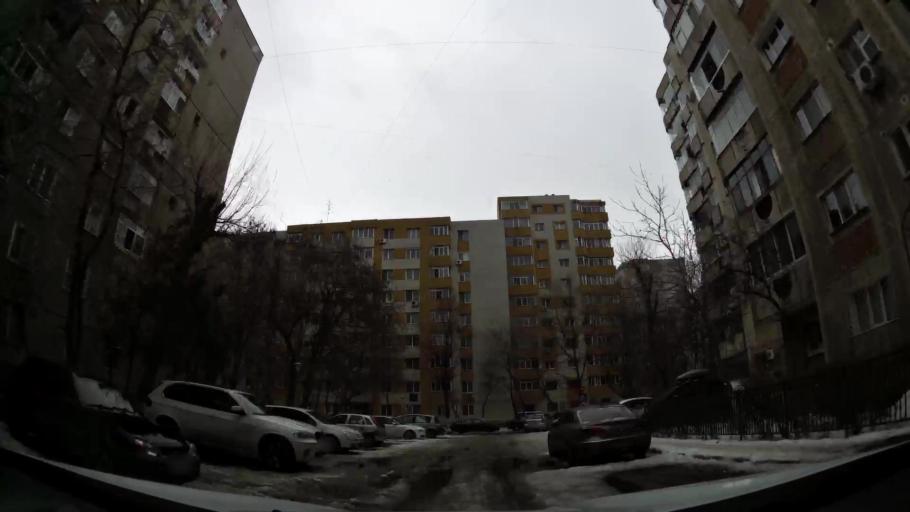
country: RO
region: Bucuresti
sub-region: Municipiul Bucuresti
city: Bucuresti
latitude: 44.4123
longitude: 26.0624
